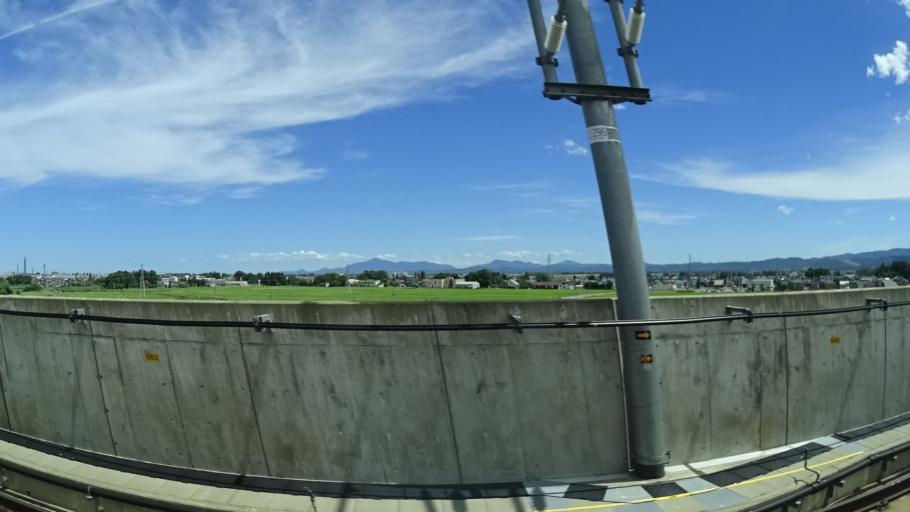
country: JP
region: Niigata
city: Joetsu
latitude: 37.0917
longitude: 138.2368
